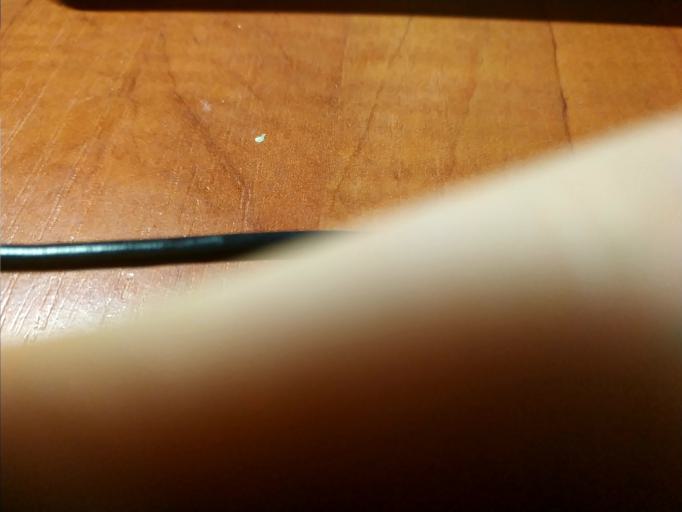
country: RU
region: Tverskaya
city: Likhoslavl'
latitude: 57.0283
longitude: 35.6134
